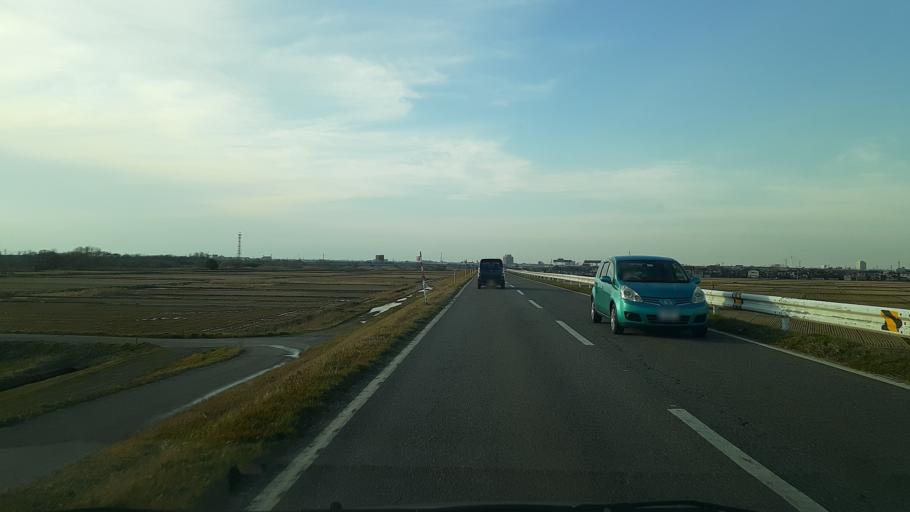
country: JP
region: Niigata
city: Niigata-shi
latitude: 37.8472
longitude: 139.0295
